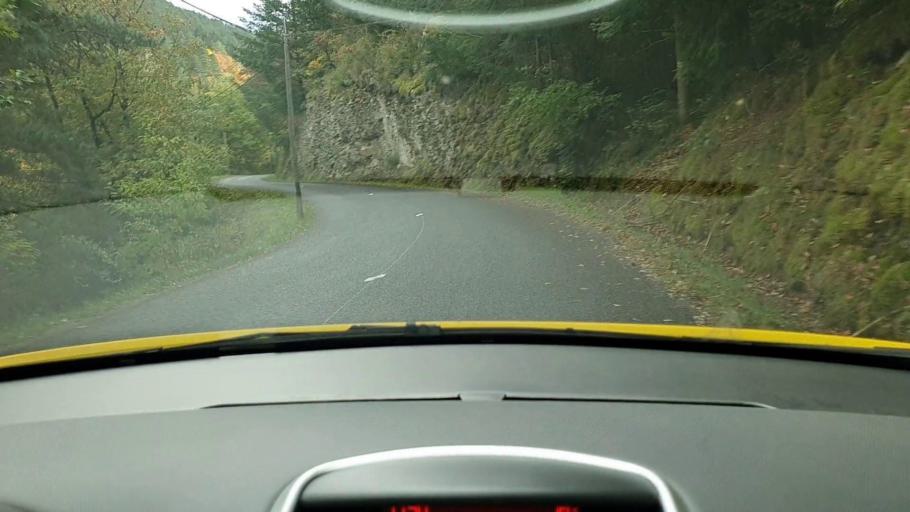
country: FR
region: Languedoc-Roussillon
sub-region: Departement de la Lozere
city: Meyrueis
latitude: 44.1117
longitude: 3.4360
